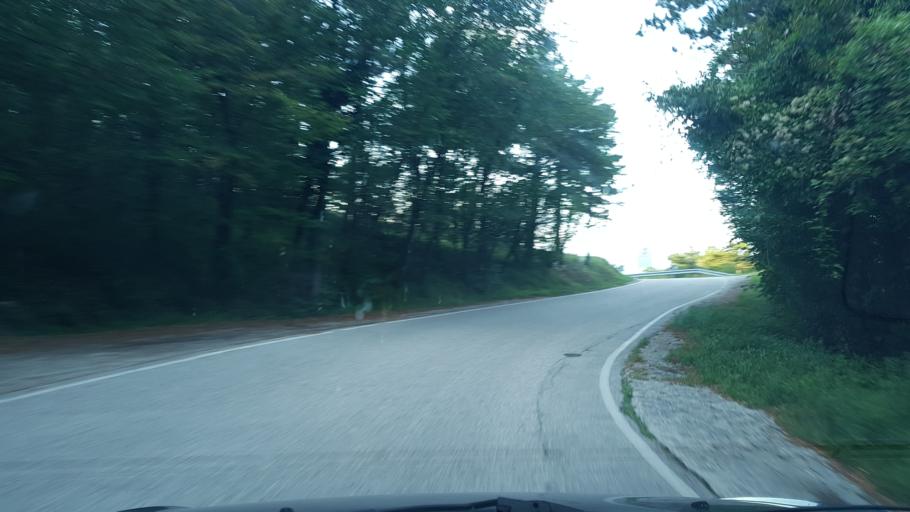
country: SI
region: Rence-Vogrsko
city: Rence
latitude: 45.8638
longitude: 13.6645
